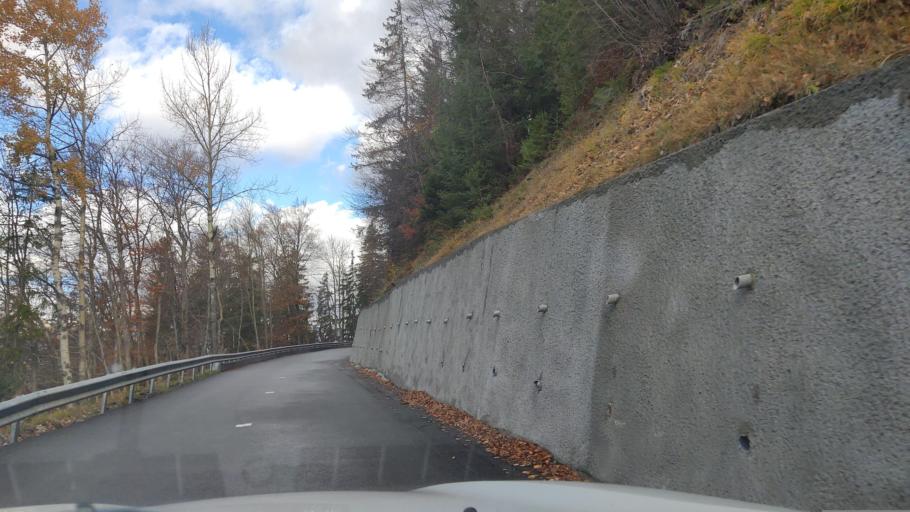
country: FR
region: Rhone-Alpes
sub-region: Departement de la Savoie
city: Saint-Jean-de-Maurienne
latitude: 45.2227
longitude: 6.3224
